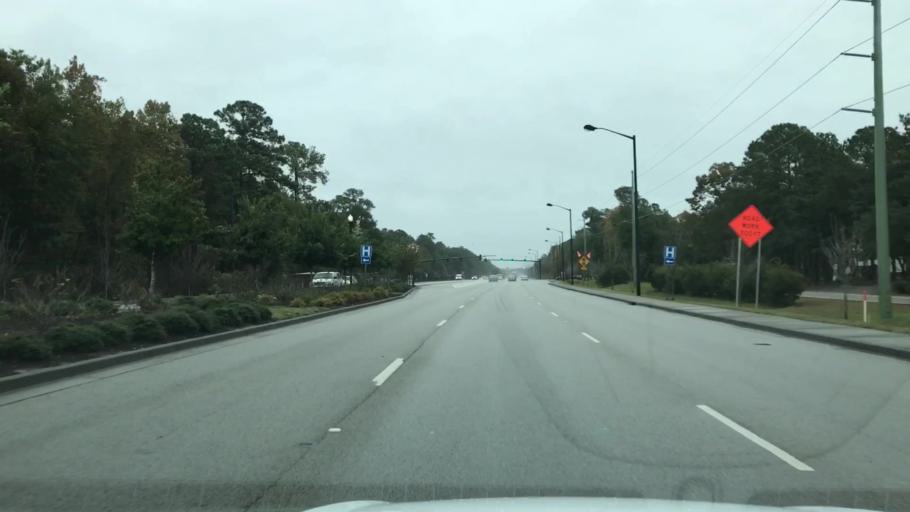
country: US
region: South Carolina
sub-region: Charleston County
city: Isle of Palms
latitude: 32.8740
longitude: -79.7732
